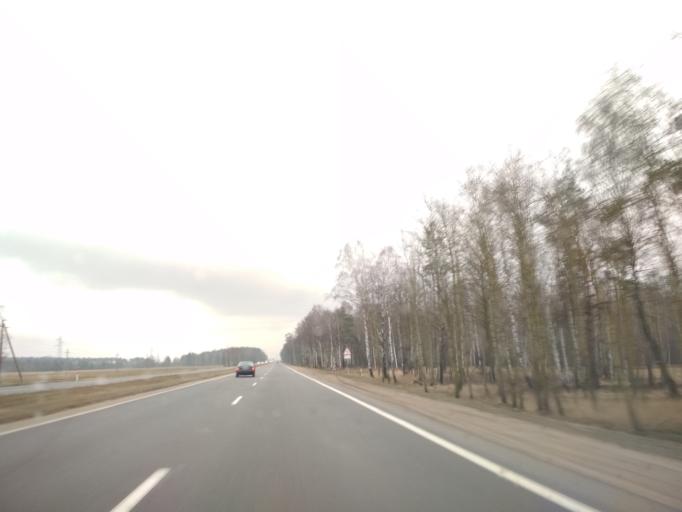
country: BY
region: Minsk
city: Dukora
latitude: 53.6290
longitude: 28.0265
